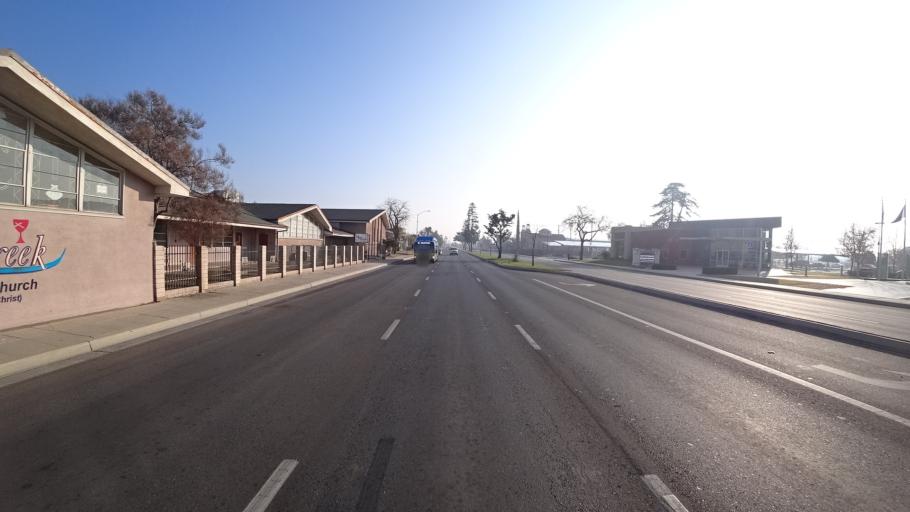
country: US
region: California
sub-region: Kern County
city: Bakersfield
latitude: 35.3733
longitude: -119.0081
